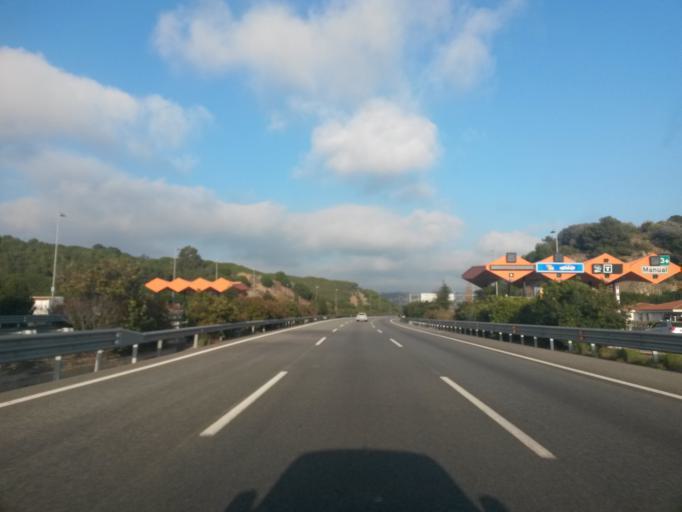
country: ES
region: Catalonia
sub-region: Provincia de Barcelona
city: Caldes d'Estrac
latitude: 41.5804
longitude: 2.5311
